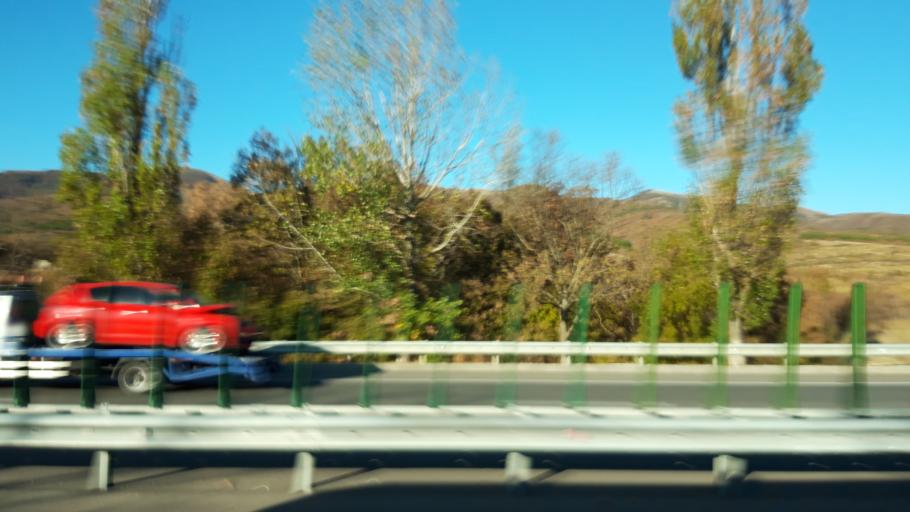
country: RU
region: Krasnodarskiy
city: Kabardinka
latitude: 44.6432
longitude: 37.9707
